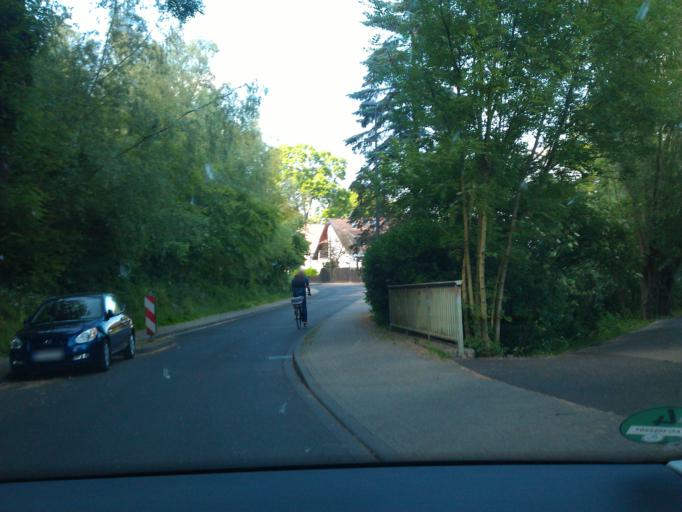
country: DE
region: North Rhine-Westphalia
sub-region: Regierungsbezirk Koln
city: Aachen
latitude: 50.7952
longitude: 6.0531
